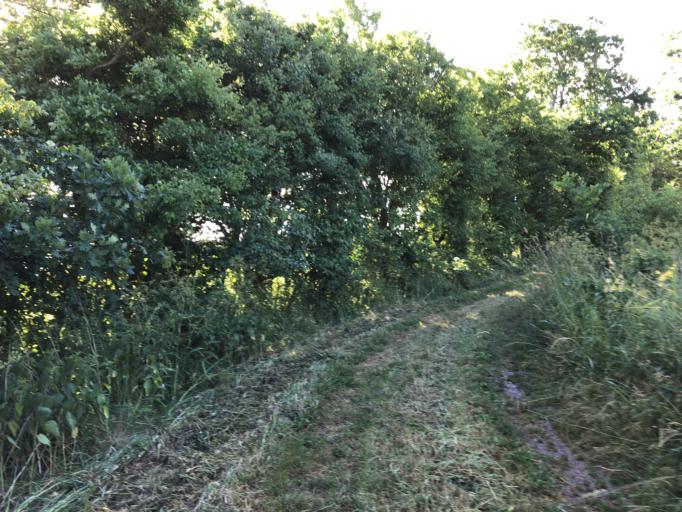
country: DK
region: Central Jutland
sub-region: Holstebro Kommune
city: Ulfborg
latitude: 56.3450
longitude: 8.2552
